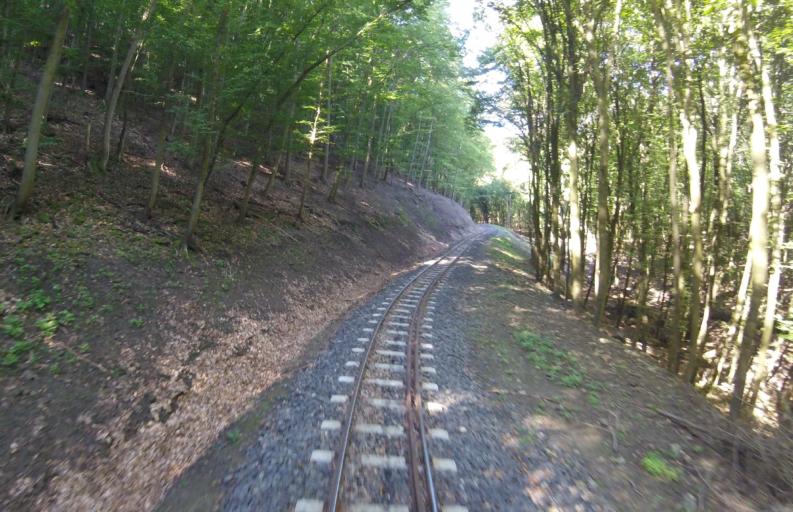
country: HU
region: Pest
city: Szob
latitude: 47.8854
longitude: 18.8667
